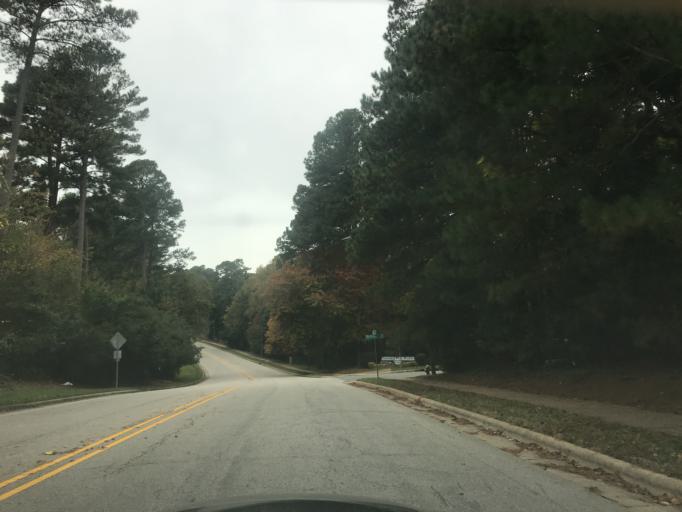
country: US
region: North Carolina
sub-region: Wake County
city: West Raleigh
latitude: 35.8846
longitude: -78.6699
